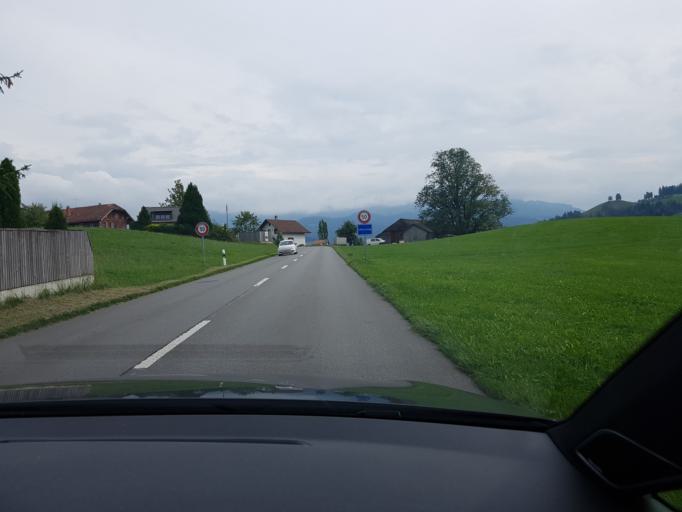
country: CH
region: Bern
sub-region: Thun District
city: Buchholterberg
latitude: 46.7948
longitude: 7.7111
